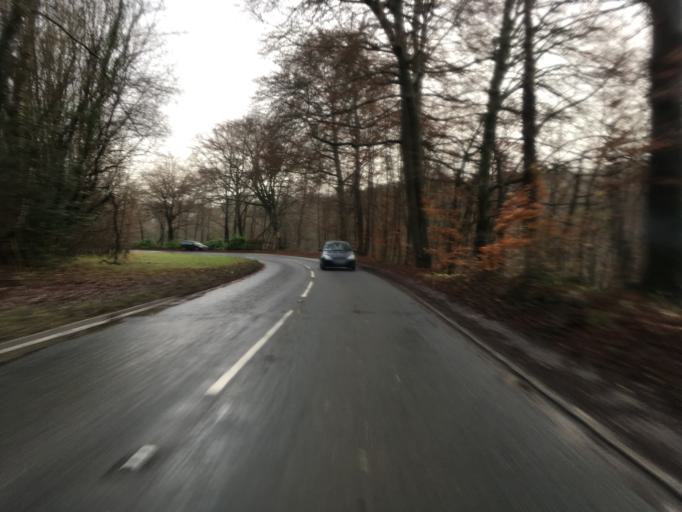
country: GB
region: England
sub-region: Gloucestershire
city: Minchinhampton
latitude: 51.6903
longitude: -2.1891
